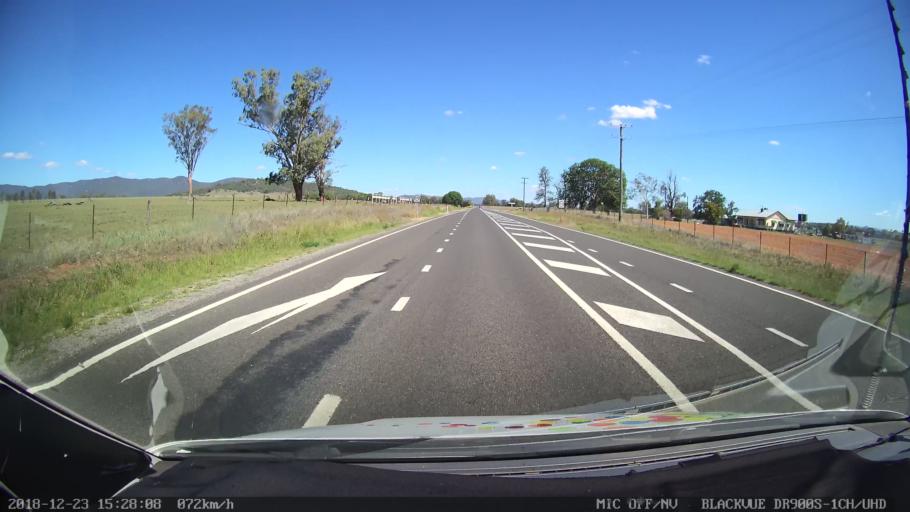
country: AU
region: New South Wales
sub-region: Tamworth Municipality
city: East Tamworth
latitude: -30.9334
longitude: 150.8501
